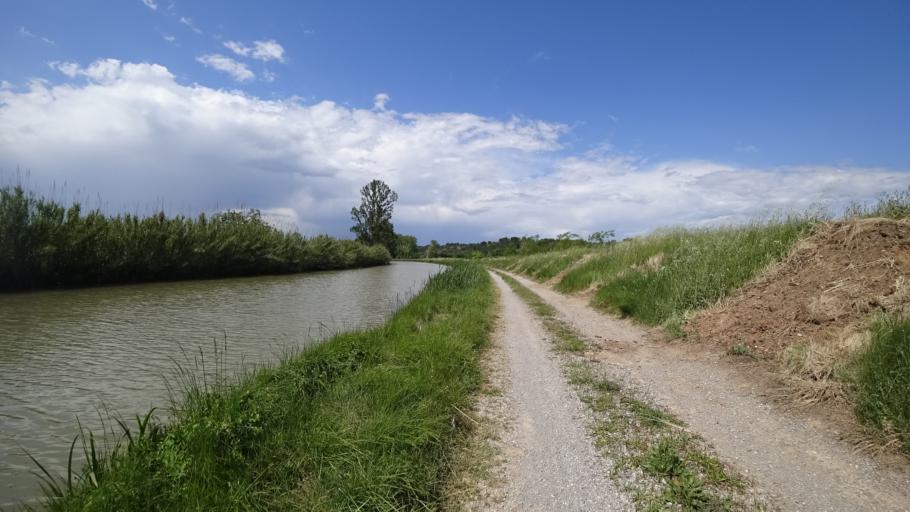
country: FR
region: Languedoc-Roussillon
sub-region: Departement de l'Aude
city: Canet
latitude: 43.2491
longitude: 2.8398
